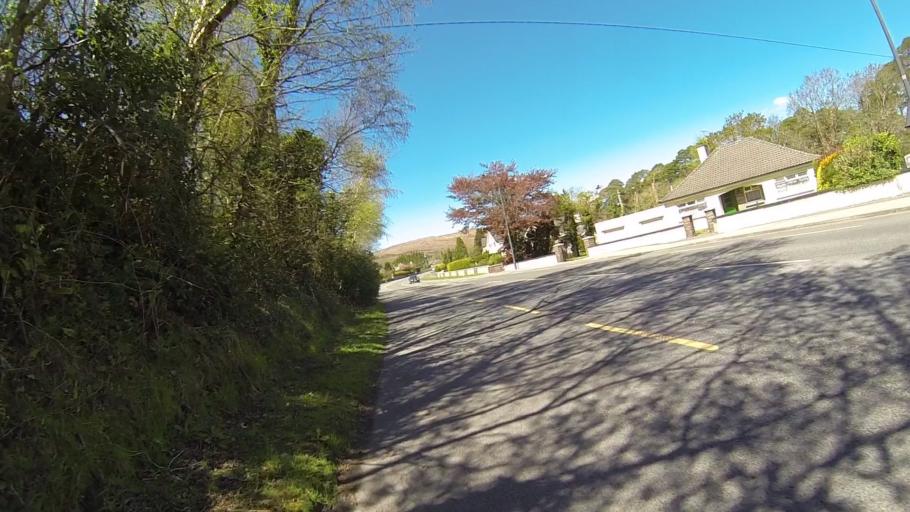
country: IE
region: Munster
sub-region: Ciarrai
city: Kenmare
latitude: 51.8851
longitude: -9.5932
